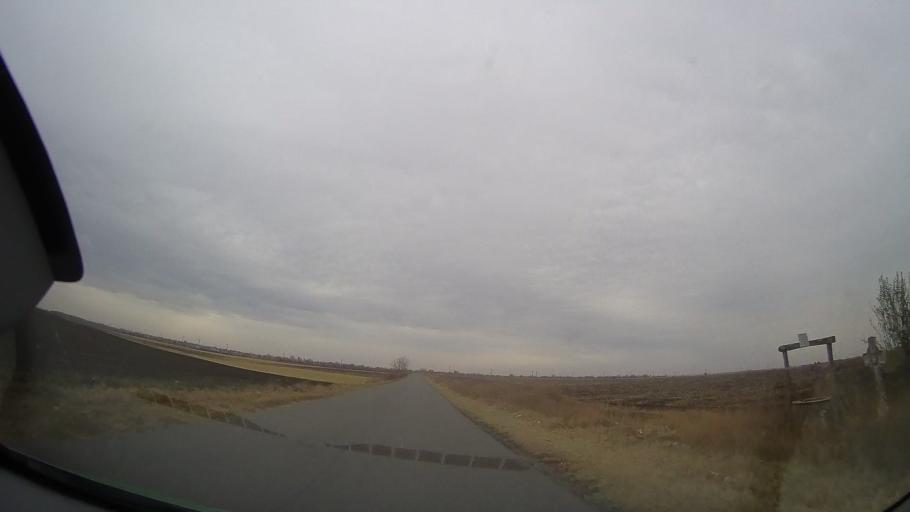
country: RO
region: Prahova
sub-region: Comuna Fantanele
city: Fantanele
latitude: 45.0106
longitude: 26.3523
